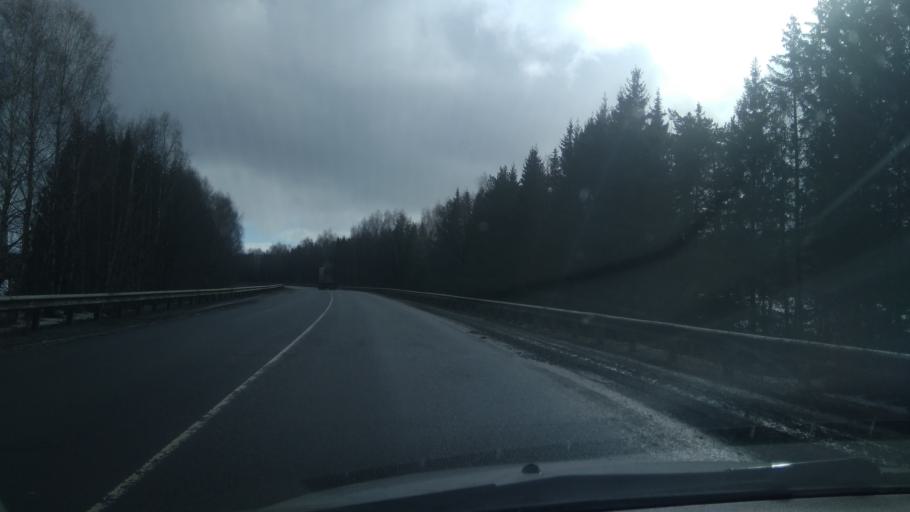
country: RU
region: Perm
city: Kukushtan
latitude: 57.4848
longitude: 56.6726
